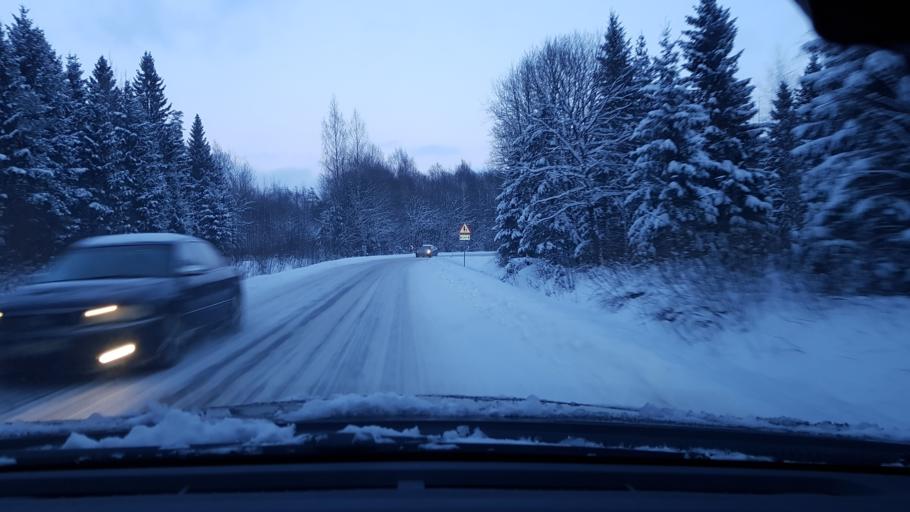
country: EE
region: Raplamaa
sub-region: Jaervakandi vald
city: Jarvakandi
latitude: 58.7961
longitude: 24.9062
